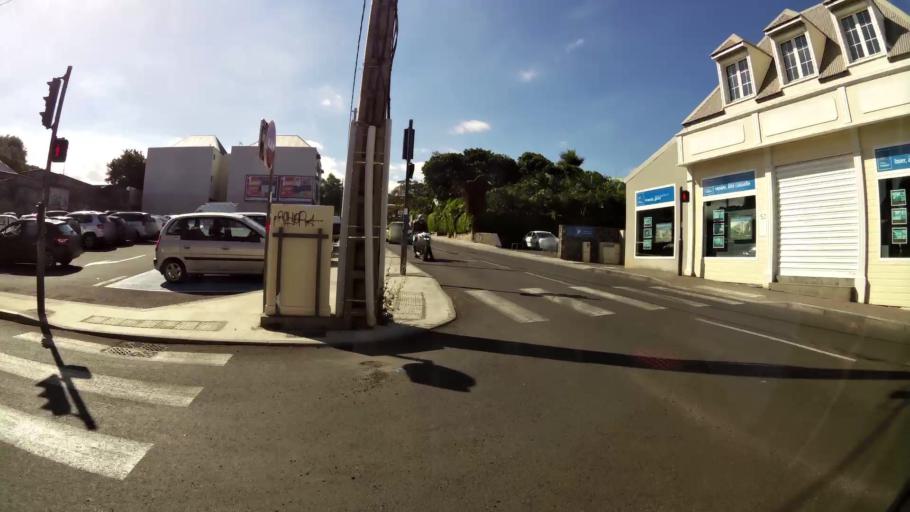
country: RE
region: Reunion
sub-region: Reunion
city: Saint-Pierre
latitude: -21.3390
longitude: 55.4793
